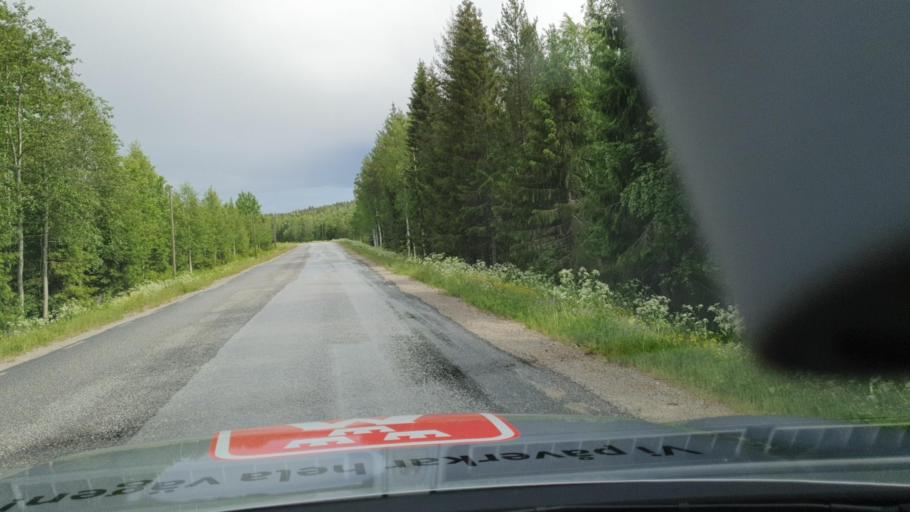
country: SE
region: Vaesternorrland
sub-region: OErnskoeldsviks Kommun
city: Bredbyn
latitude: 63.3296
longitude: 18.0921
